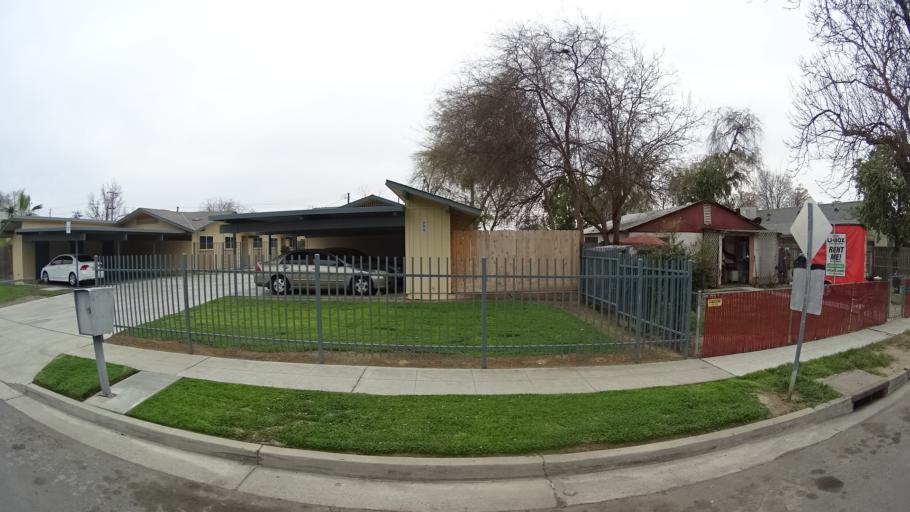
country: US
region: California
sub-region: Fresno County
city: Fresno
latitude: 36.8383
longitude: -119.7963
